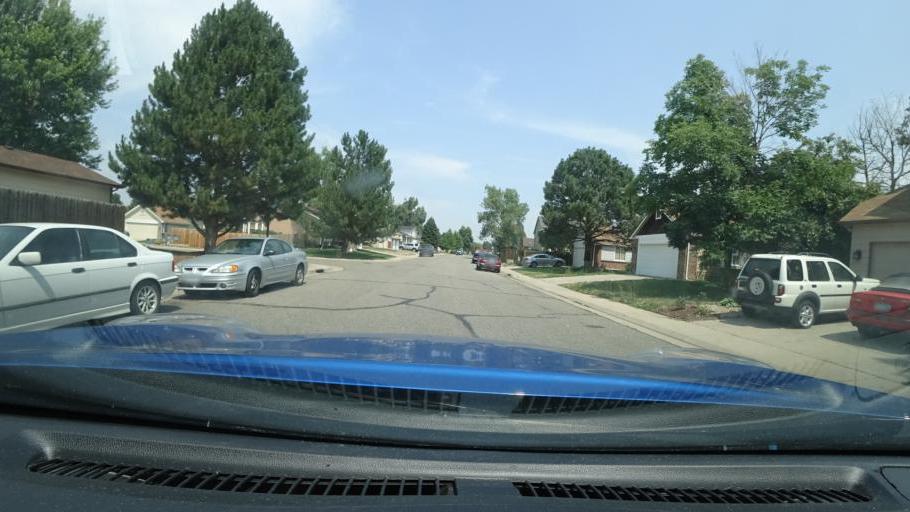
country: US
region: Colorado
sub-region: Adams County
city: Aurora
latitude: 39.7767
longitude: -104.7579
